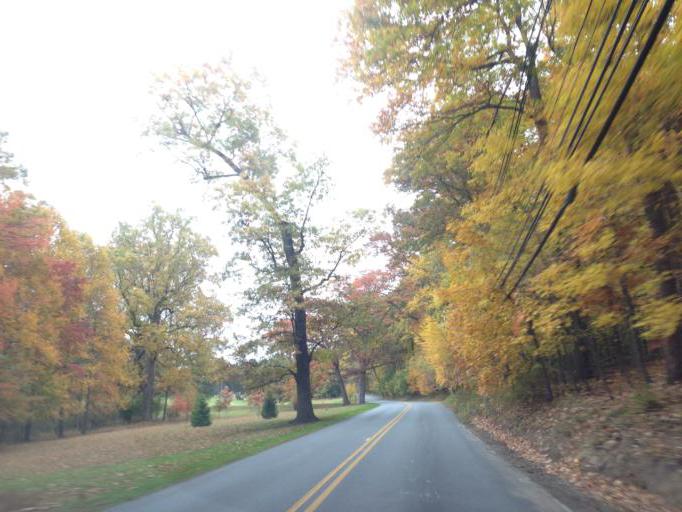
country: US
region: Maryland
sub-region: Baltimore County
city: Owings Mills
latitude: 39.4179
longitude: -76.7670
